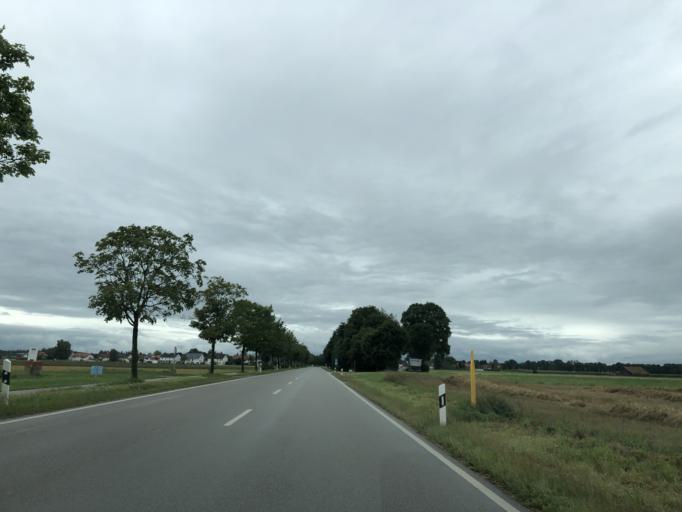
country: DE
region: Bavaria
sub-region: Upper Bavaria
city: Sauerlach
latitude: 47.9854
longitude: 11.6473
